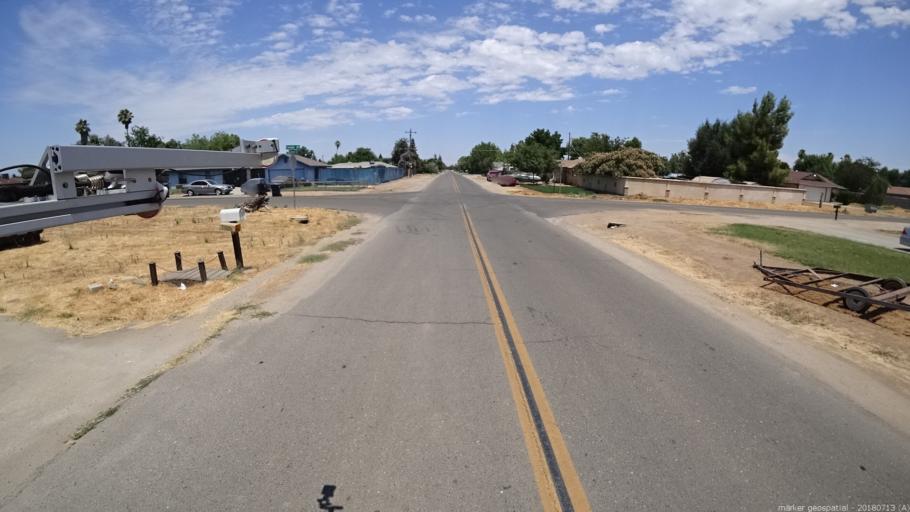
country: US
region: California
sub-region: Madera County
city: Madera Acres
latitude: 36.9916
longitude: -120.0804
